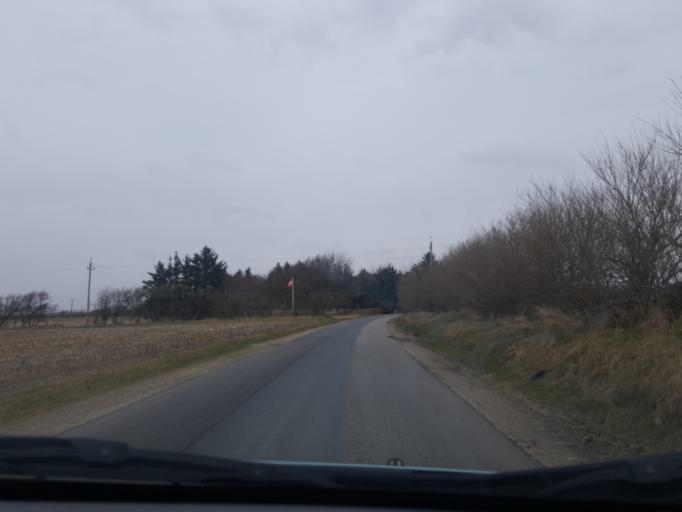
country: DK
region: Central Jutland
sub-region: Holstebro Kommune
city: Ulfborg
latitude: 56.2181
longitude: 8.2615
